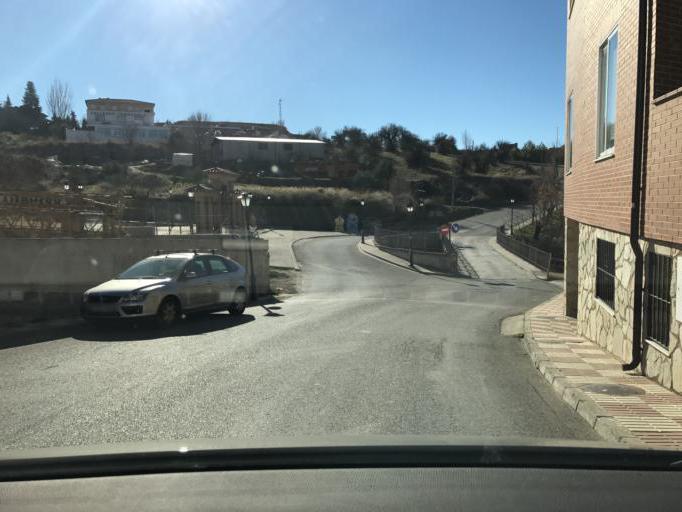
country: ES
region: Andalusia
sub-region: Provincia de Granada
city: Alfacar
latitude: 37.2357
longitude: -3.5691
